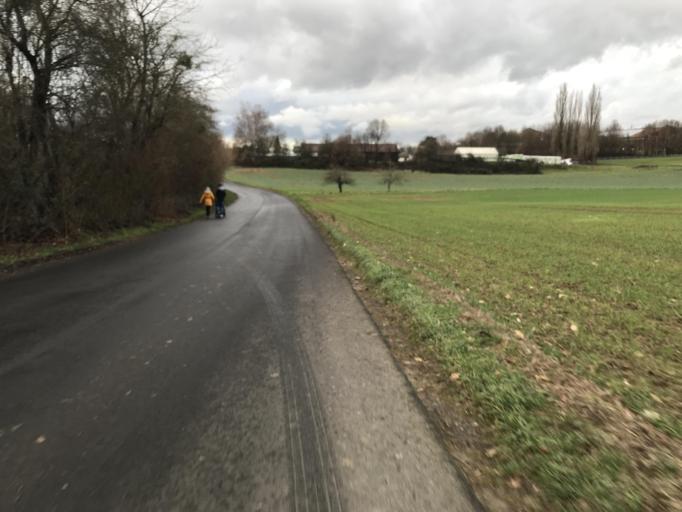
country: DE
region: Hesse
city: Budingen
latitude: 50.2778
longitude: 9.1178
